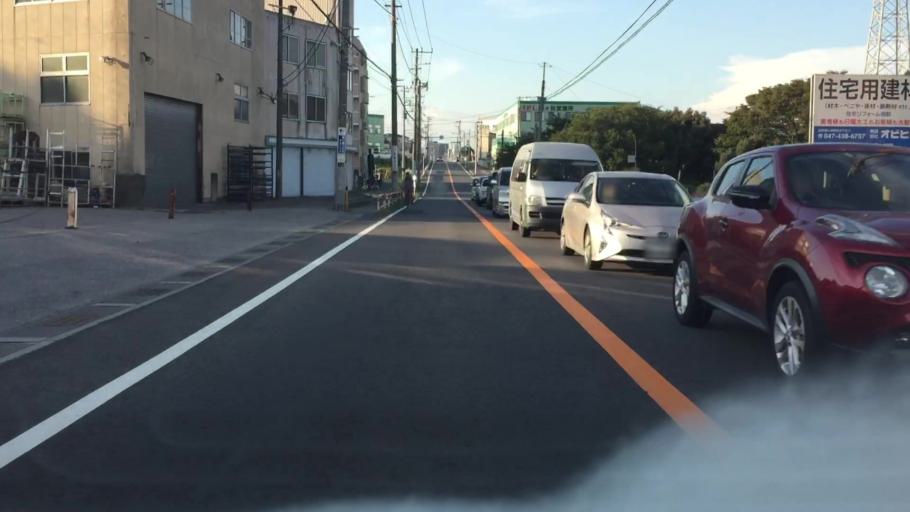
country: JP
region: Chiba
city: Funabashi
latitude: 35.7502
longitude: 139.9988
